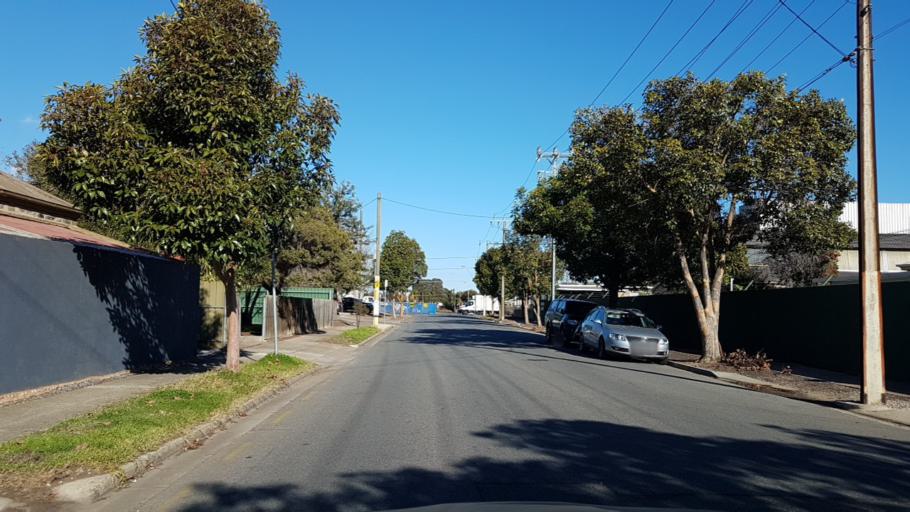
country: AU
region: South Australia
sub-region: City of West Torrens
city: Plympton
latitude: -34.9591
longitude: 138.5455
